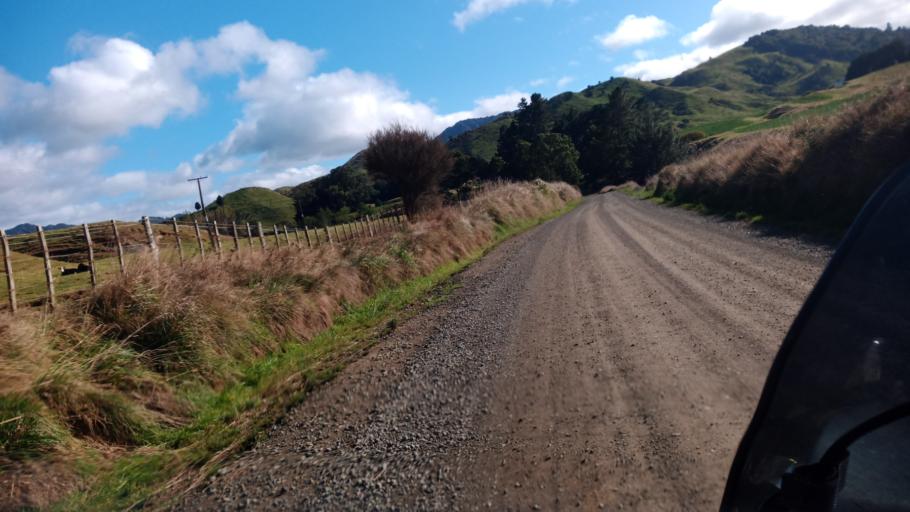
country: NZ
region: Bay of Plenty
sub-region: Opotiki District
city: Opotiki
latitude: -38.4658
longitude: 177.4270
